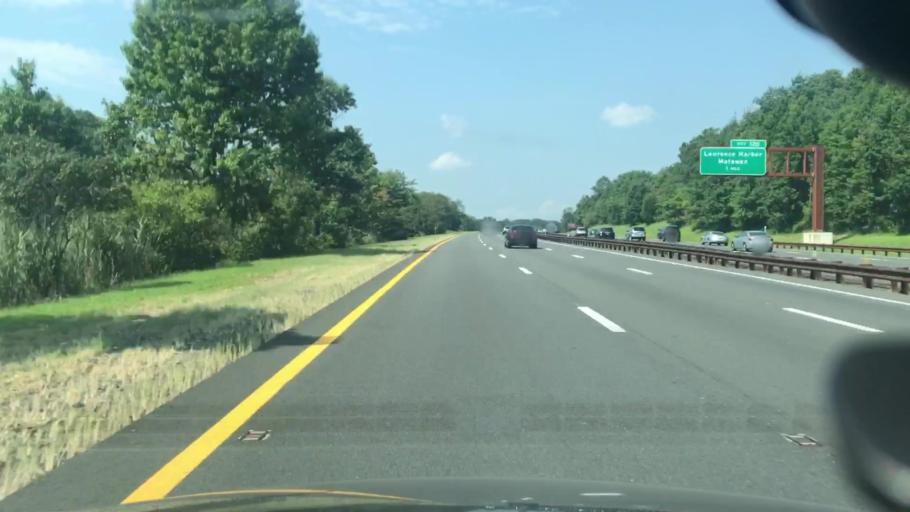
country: US
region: New Jersey
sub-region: Monmouth County
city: Matawan
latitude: 40.4289
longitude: -74.2349
